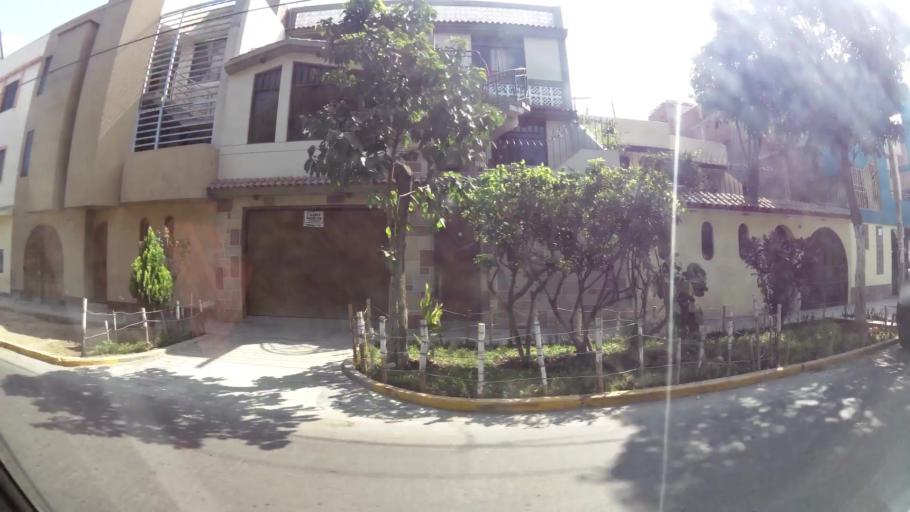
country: PE
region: La Libertad
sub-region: Provincia de Trujillo
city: Trujillo
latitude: -8.1233
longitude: -79.0393
